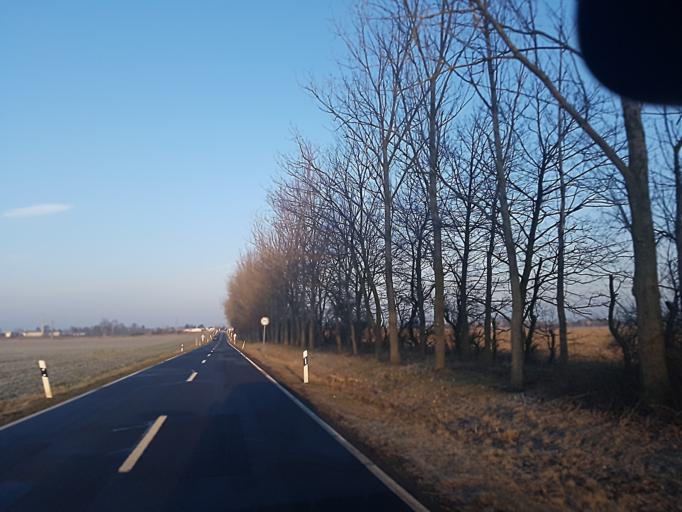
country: DE
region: Brandenburg
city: Juterbog
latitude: 51.9259
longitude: 13.0564
